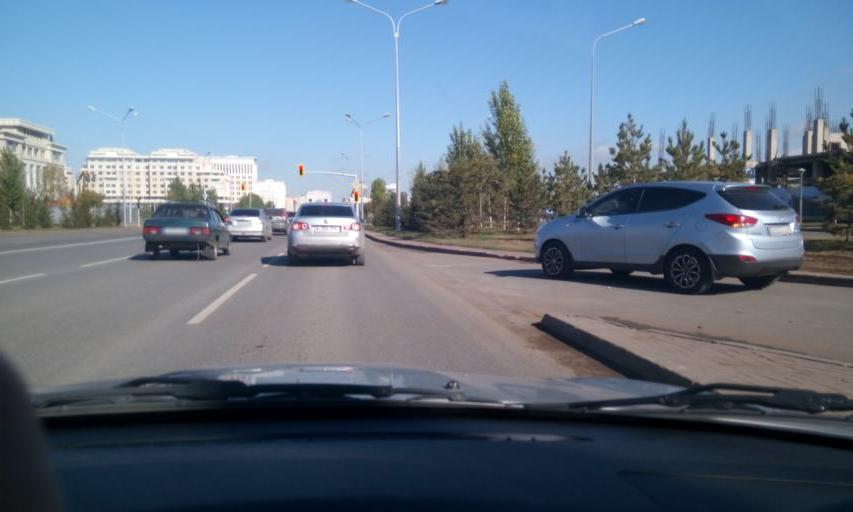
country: KZ
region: Astana Qalasy
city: Astana
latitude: 51.0990
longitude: 71.4283
